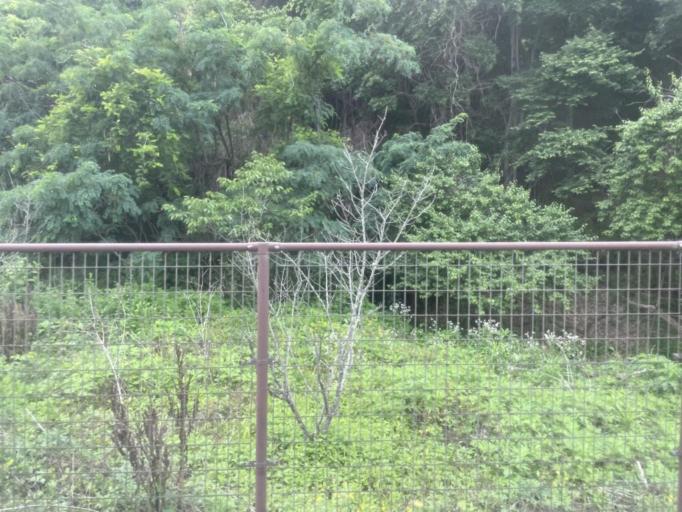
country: JP
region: Gunma
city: Takasaki
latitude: 36.2845
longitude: 139.0292
